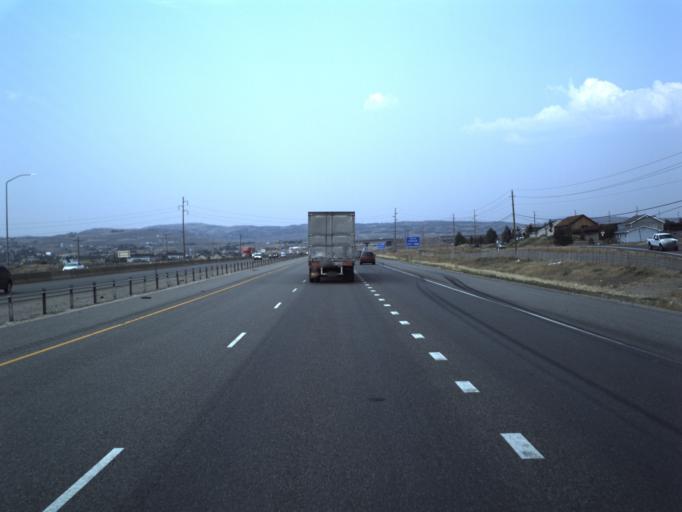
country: US
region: Utah
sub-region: Summit County
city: Snyderville
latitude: 40.7250
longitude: -111.5116
